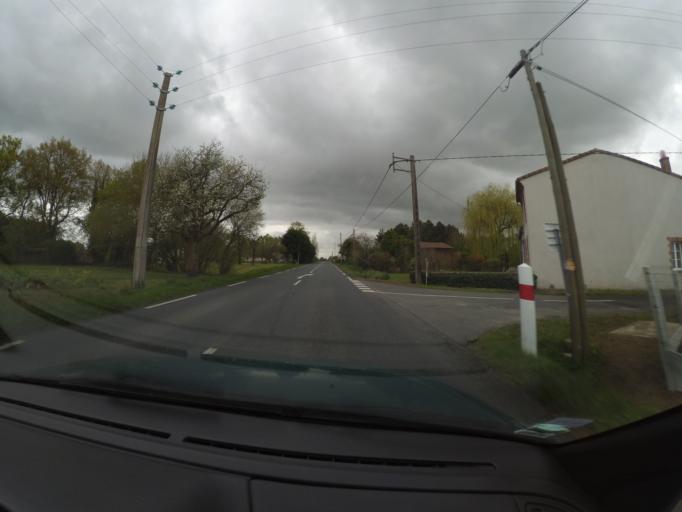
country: FR
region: Pays de la Loire
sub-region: Departement de la Loire-Atlantique
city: La Remaudiere
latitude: 47.2098
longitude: -1.2405
